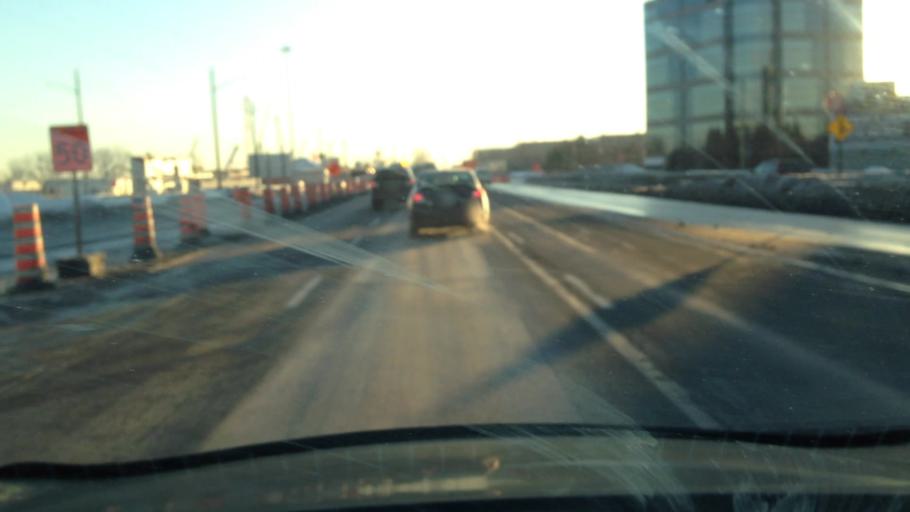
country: CA
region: Quebec
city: Westmount
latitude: 45.4700
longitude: -73.5414
